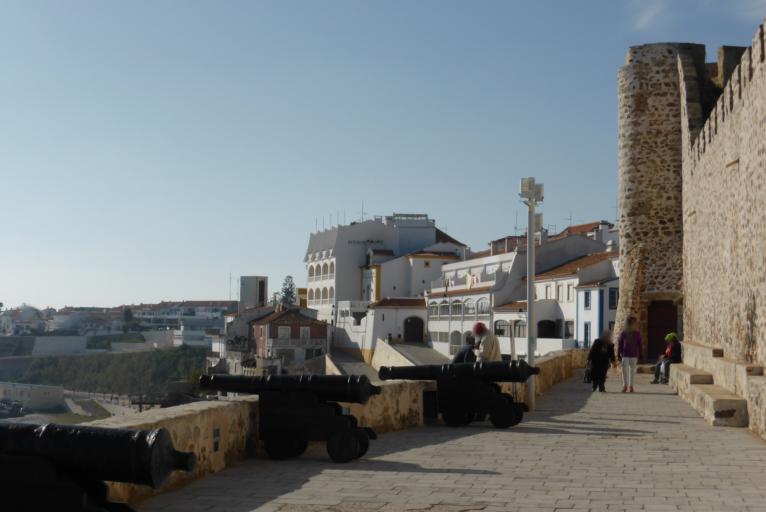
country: PT
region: Setubal
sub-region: Sines
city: Sines
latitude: 37.9547
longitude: -8.8664
